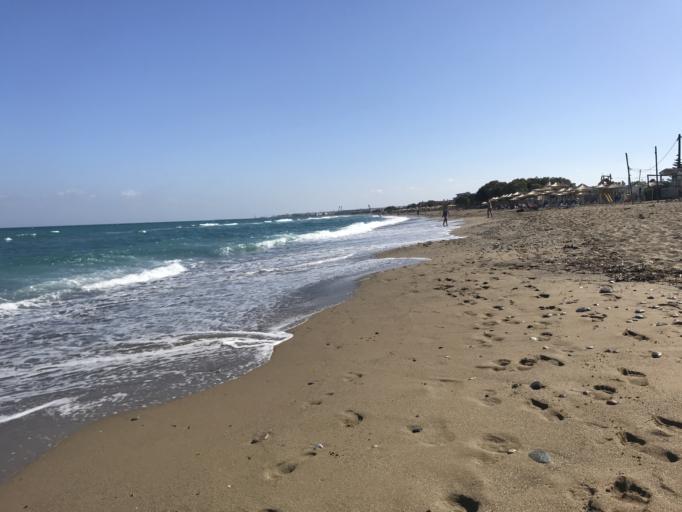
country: GR
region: Crete
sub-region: Nomos Irakleiou
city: Gazi
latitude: 35.3385
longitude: 25.0688
